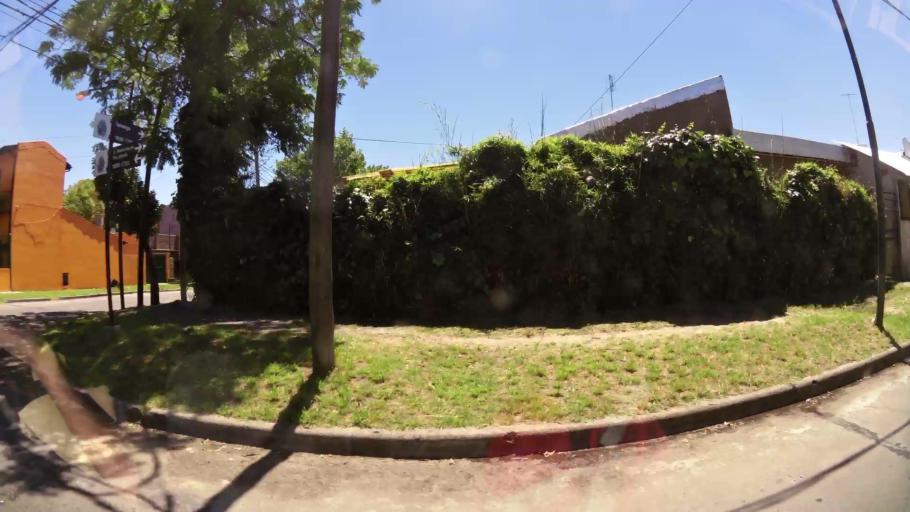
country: AR
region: Buenos Aires
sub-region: Partido de Tigre
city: Tigre
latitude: -34.4953
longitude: -58.5785
